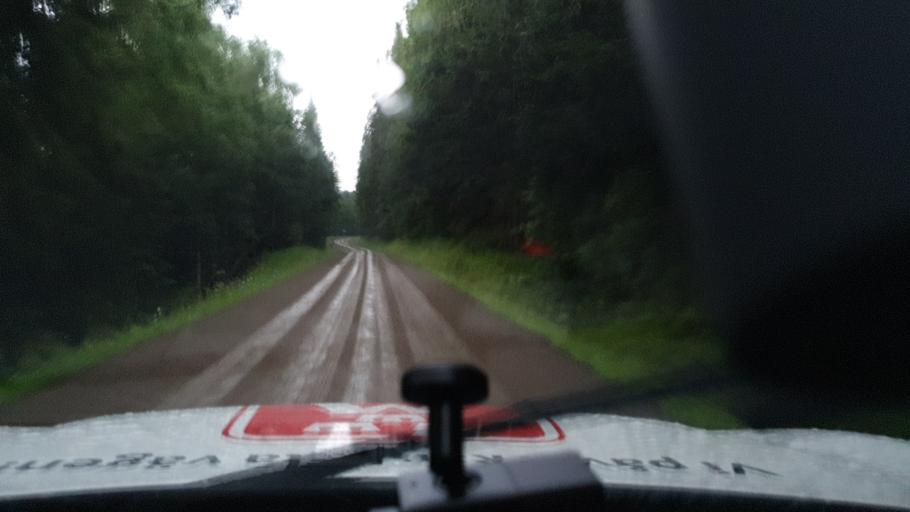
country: SE
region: Vaermland
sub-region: Hagfors Kommun
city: Ekshaerad
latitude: 60.4204
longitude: 13.2488
